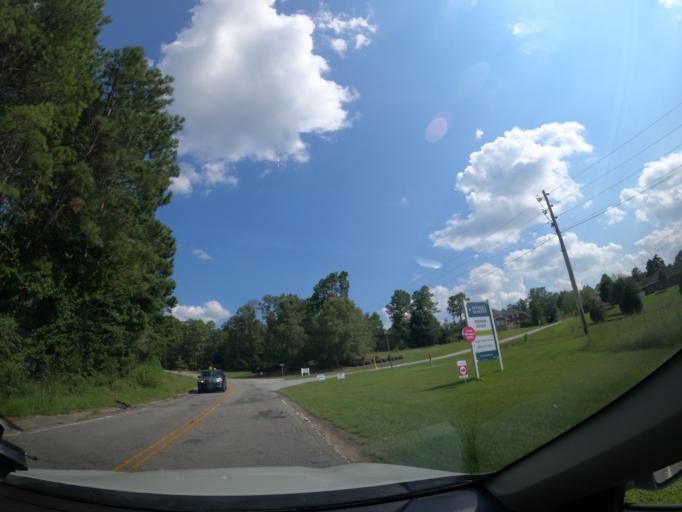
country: US
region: South Carolina
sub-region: Lexington County
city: South Congaree
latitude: 33.9074
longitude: -81.1638
